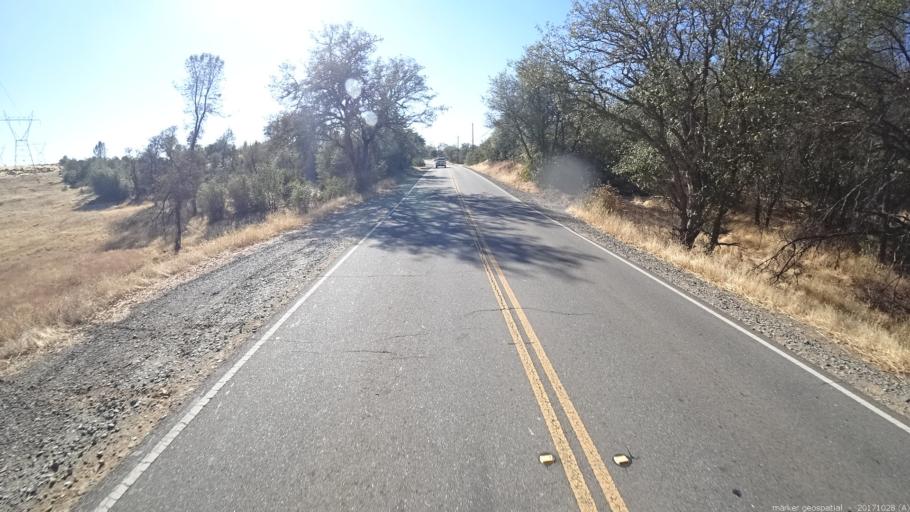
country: US
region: California
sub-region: Shasta County
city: Redding
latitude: 40.6213
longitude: -122.4247
